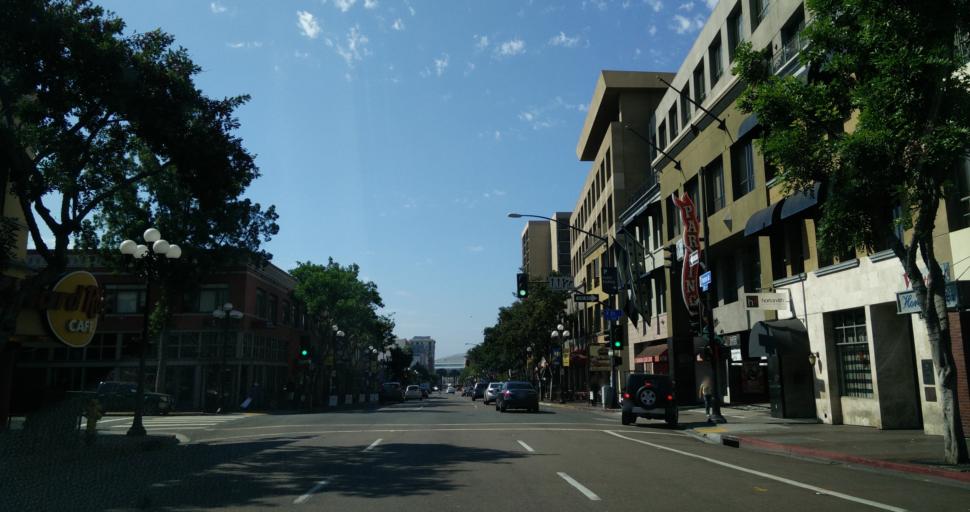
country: US
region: California
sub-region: San Diego County
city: San Diego
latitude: 32.7140
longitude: -117.1611
